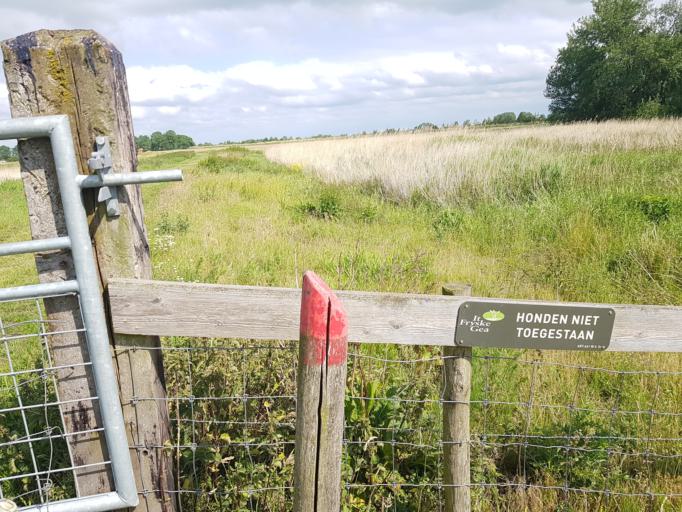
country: NL
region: Friesland
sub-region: Gemeente Boarnsterhim
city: Aldeboarn
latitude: 53.0934
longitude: 5.9083
